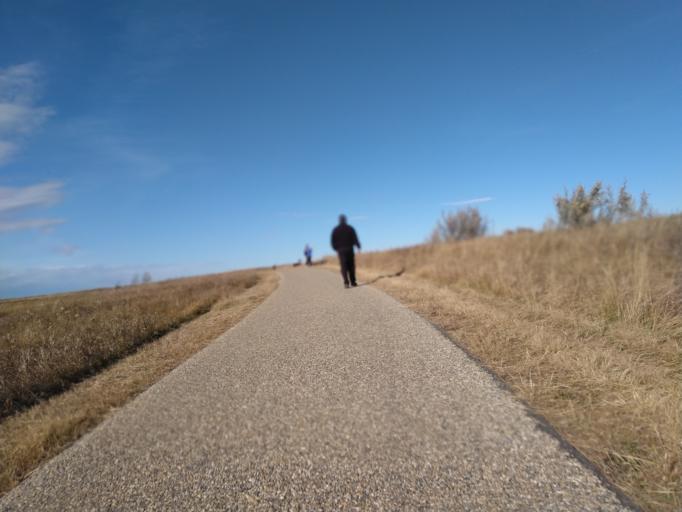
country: CA
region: Alberta
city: Calgary
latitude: 51.1063
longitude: -114.1139
